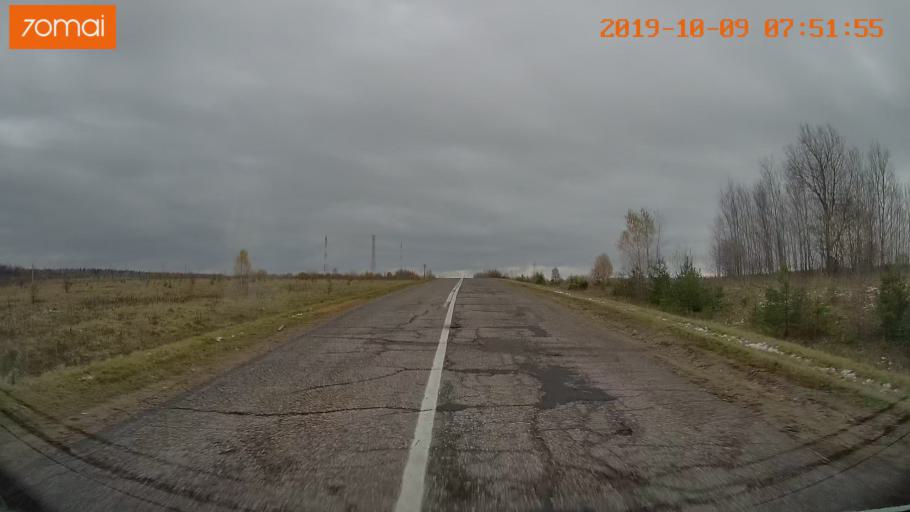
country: RU
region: Jaroslavl
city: Kukoboy
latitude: 58.6872
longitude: 39.8820
